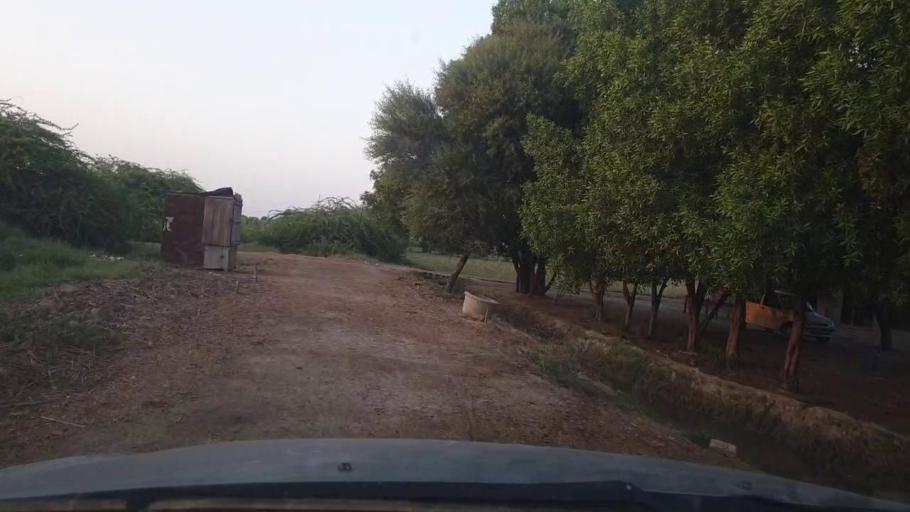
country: PK
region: Sindh
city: Tando Ghulam Ali
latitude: 25.1211
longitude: 68.9865
